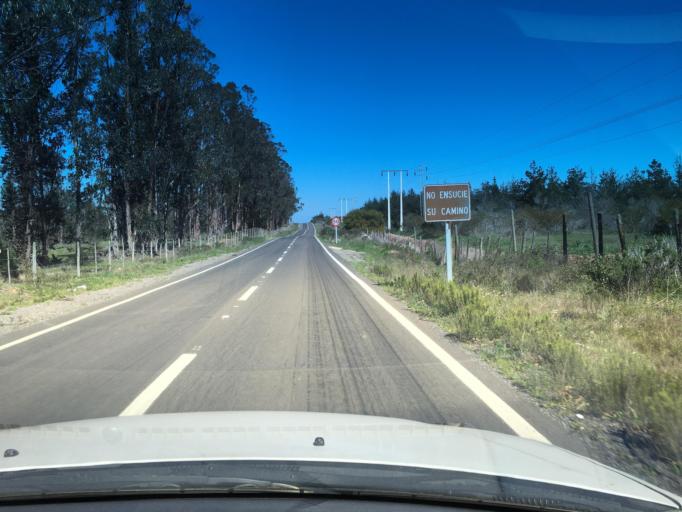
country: CL
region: Valparaiso
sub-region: San Antonio Province
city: El Tabo
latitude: -33.4040
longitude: -71.5894
